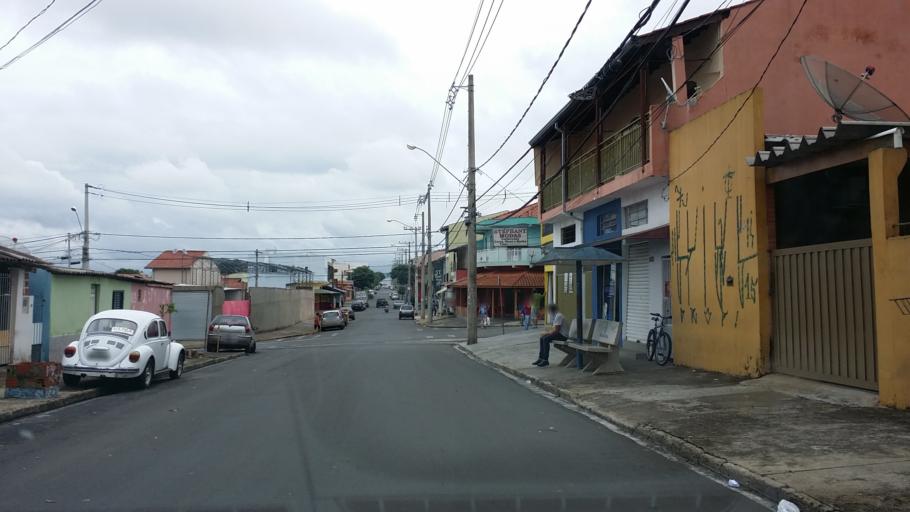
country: BR
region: Sao Paulo
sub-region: Indaiatuba
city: Indaiatuba
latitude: -23.1197
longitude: -47.2400
